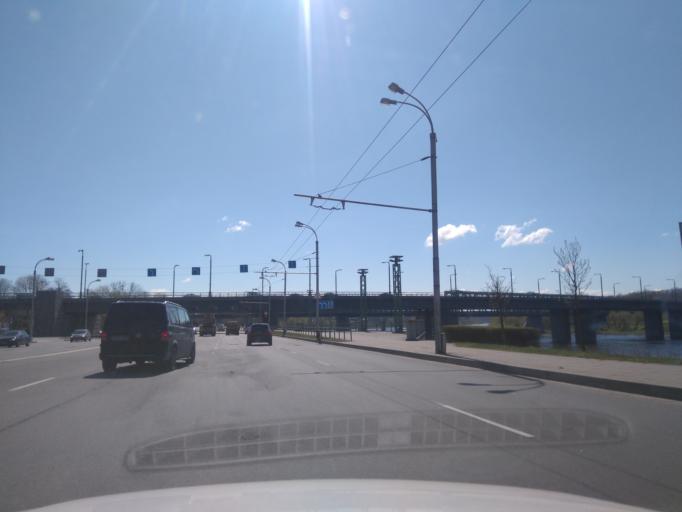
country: LT
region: Kauno apskritis
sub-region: Kaunas
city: Aleksotas
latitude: 54.8847
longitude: 23.9240
